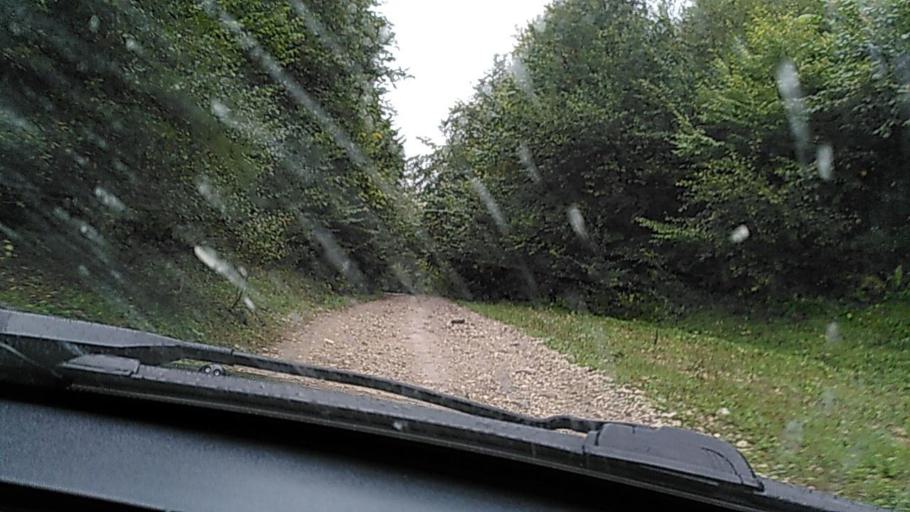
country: RU
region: Kabardino-Balkariya
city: Belaya Rechka
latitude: 43.3947
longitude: 43.4457
